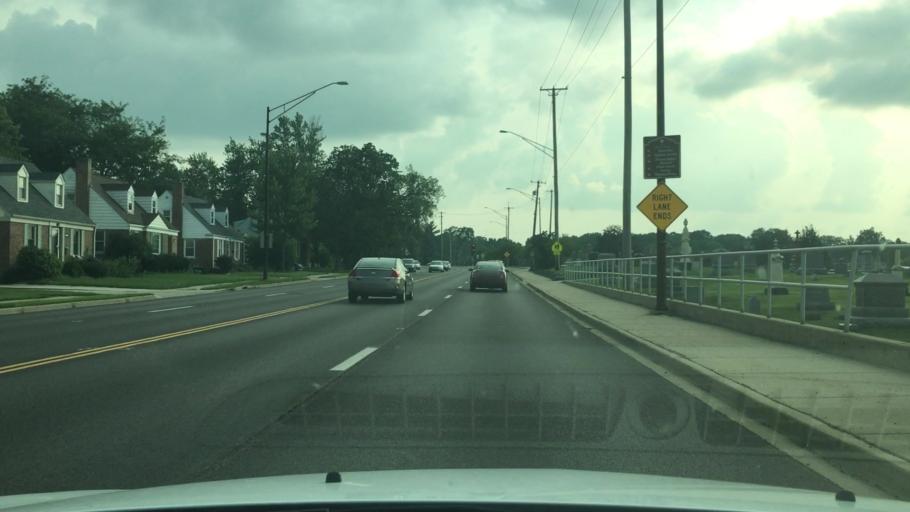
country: US
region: Illinois
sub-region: DeKalb County
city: DeKalb
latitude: 41.9382
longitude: -88.7458
